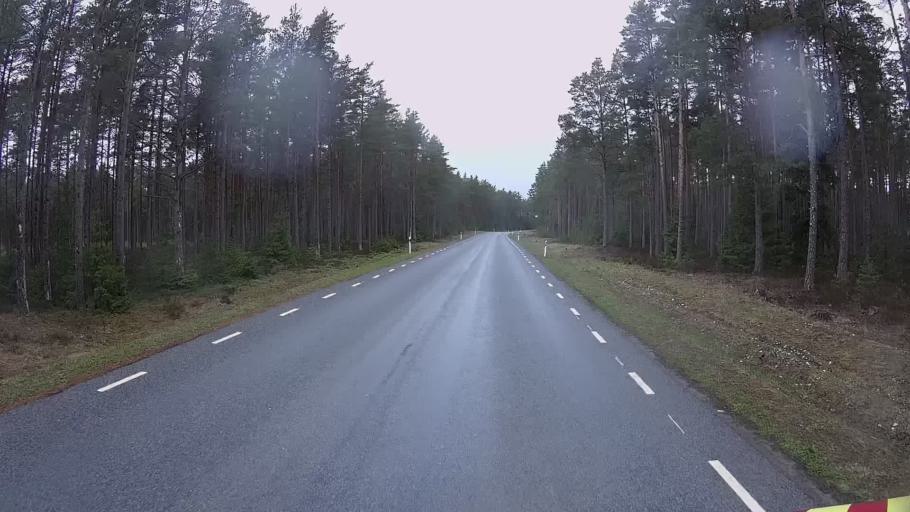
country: EE
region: Hiiumaa
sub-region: Kaerdla linn
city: Kardla
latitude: 58.9098
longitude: 22.3916
